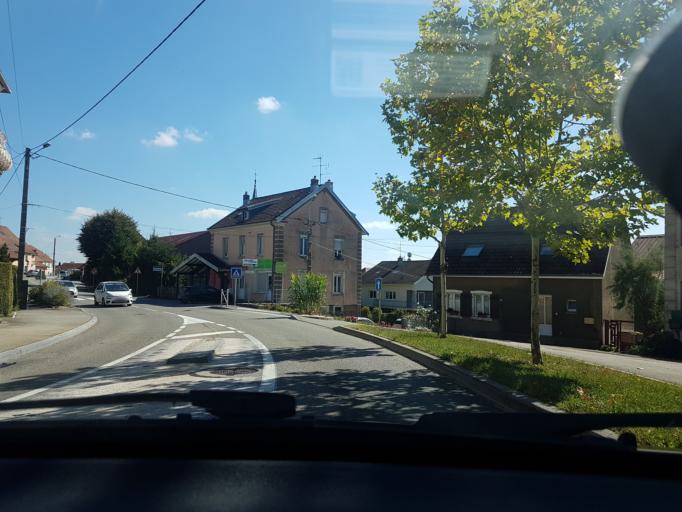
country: FR
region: Franche-Comte
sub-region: Territoire de Belfort
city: Belfort
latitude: 47.6370
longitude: 6.8908
